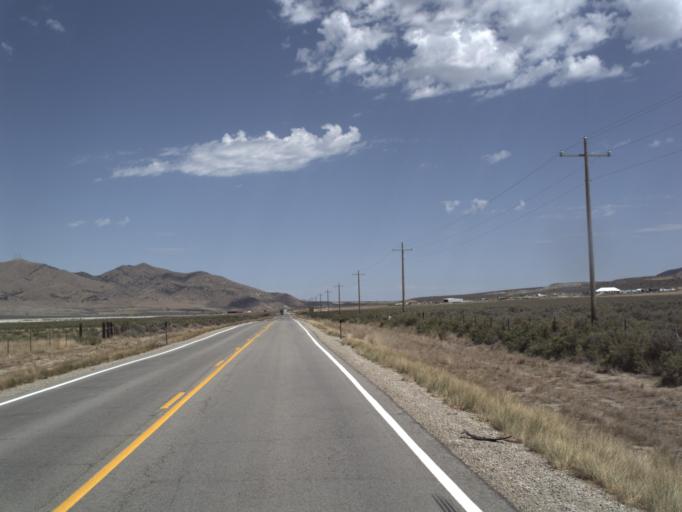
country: US
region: Utah
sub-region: Tooele County
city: Tooele
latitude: 40.3887
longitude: -112.3862
